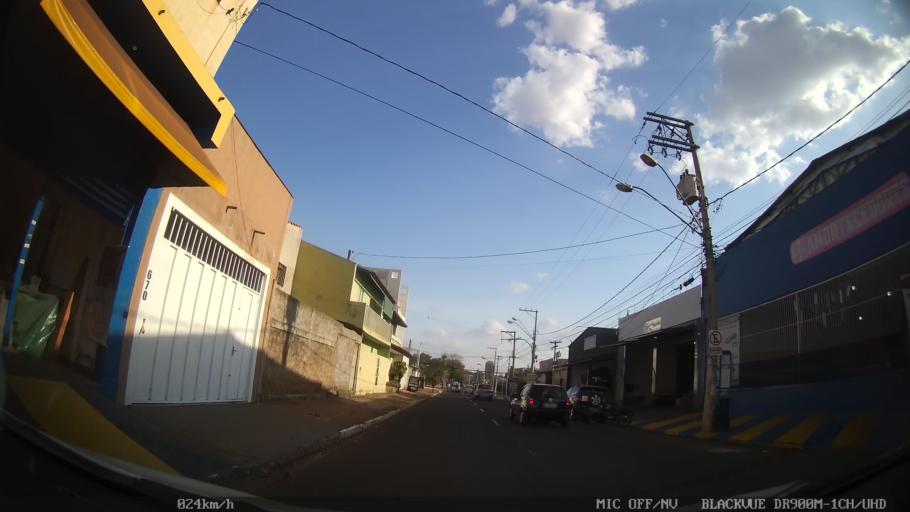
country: BR
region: Sao Paulo
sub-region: Ribeirao Preto
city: Ribeirao Preto
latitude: -21.1616
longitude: -47.8103
